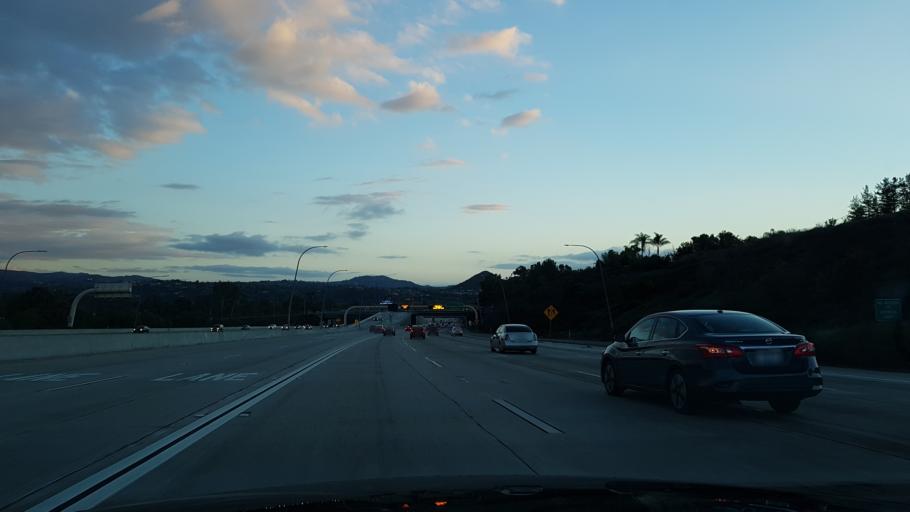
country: US
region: California
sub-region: San Diego County
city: Escondido
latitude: 33.0776
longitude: -117.0713
